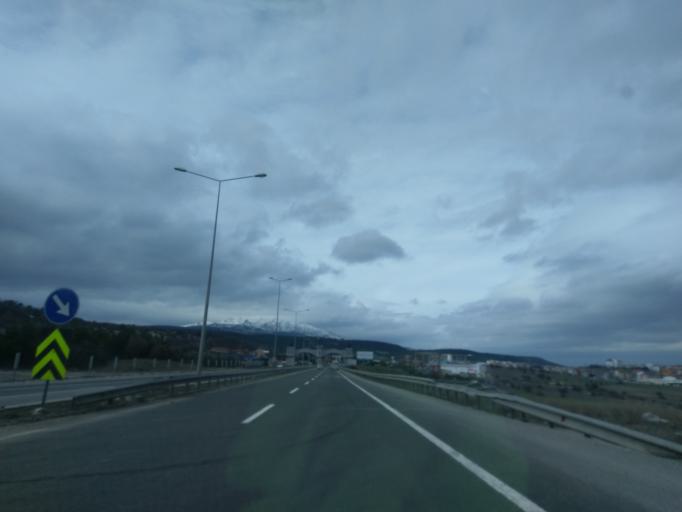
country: TR
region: Kuetahya
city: Kutahya
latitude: 39.3757
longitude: 30.0605
